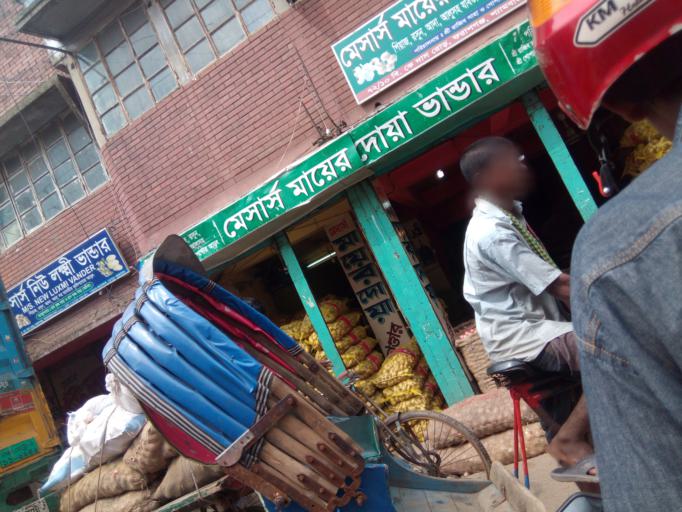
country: BD
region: Dhaka
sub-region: Dhaka
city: Dhaka
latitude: 23.7030
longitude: 90.4151
